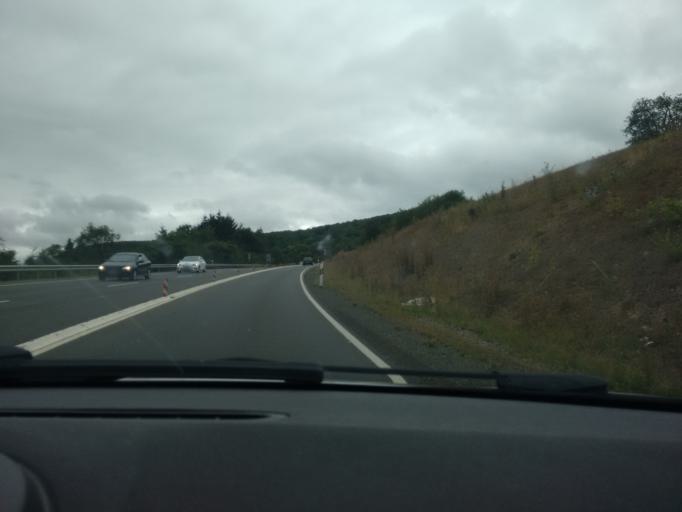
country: DE
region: Rheinland-Pfalz
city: Waldbockelheim
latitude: 49.8161
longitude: 7.7122
